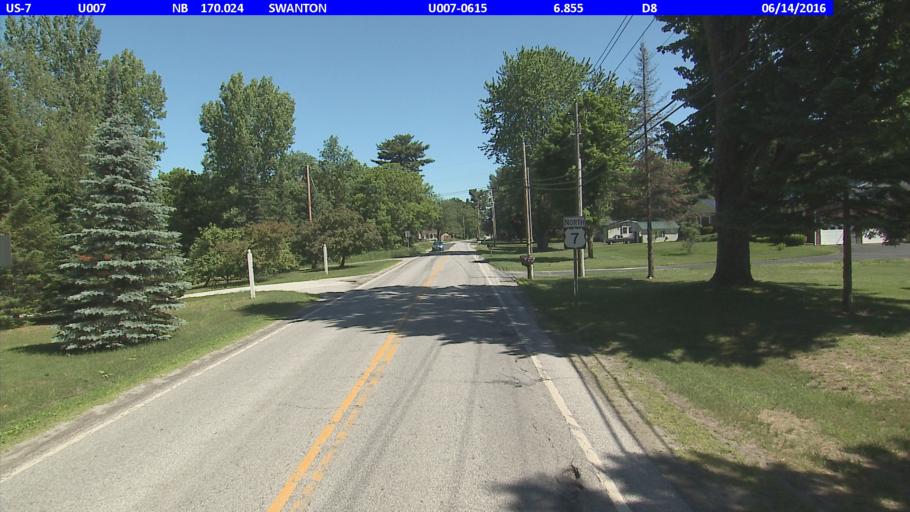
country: US
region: Vermont
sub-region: Franklin County
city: Swanton
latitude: 44.9318
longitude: -73.1194
